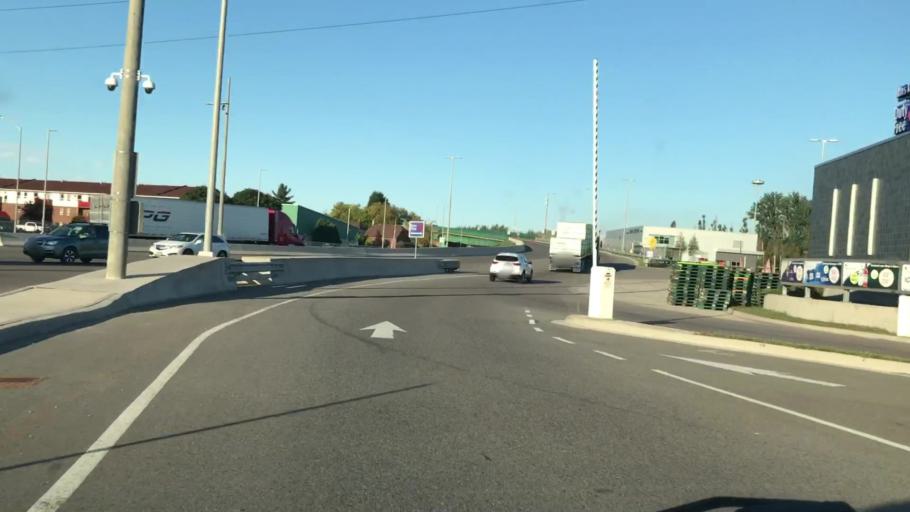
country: CA
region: Ontario
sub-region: Algoma
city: Sault Ste. Marie
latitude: 46.5195
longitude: -84.3502
